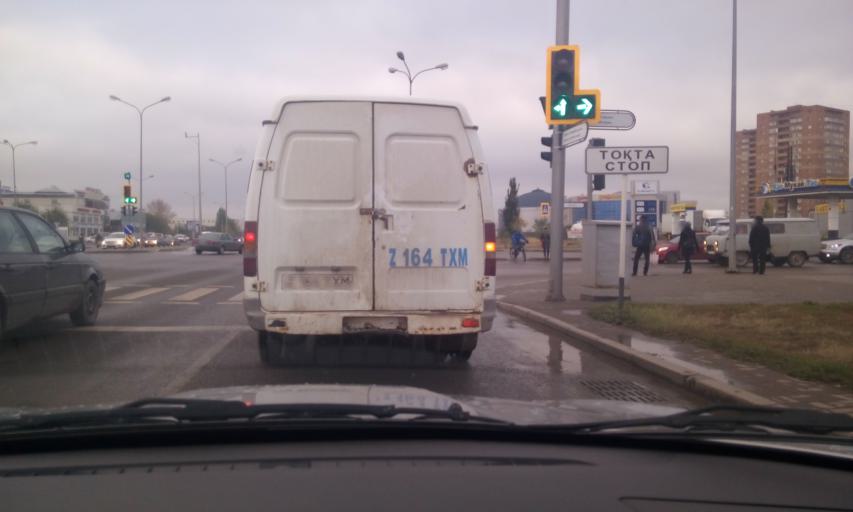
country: KZ
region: Astana Qalasy
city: Astana
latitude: 51.1814
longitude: 71.3737
